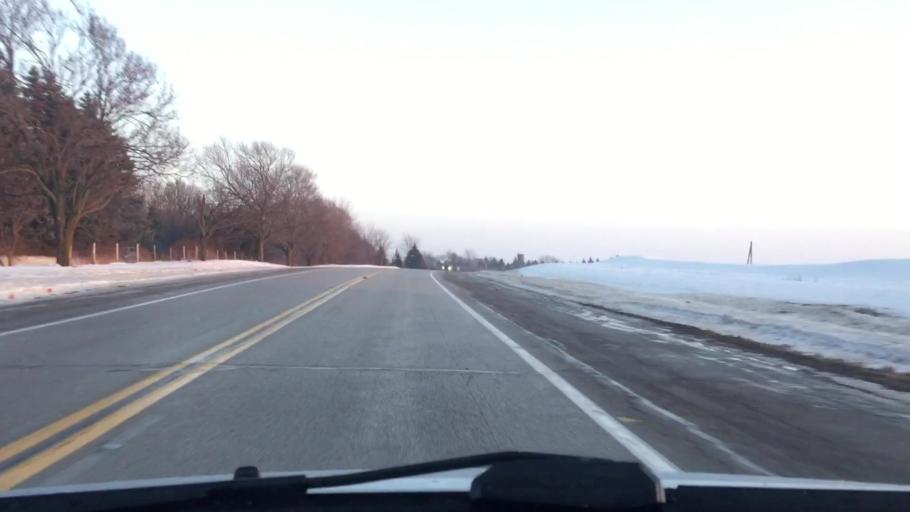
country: US
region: Illinois
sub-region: Kane County
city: Wasco
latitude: 41.9453
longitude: -88.4012
